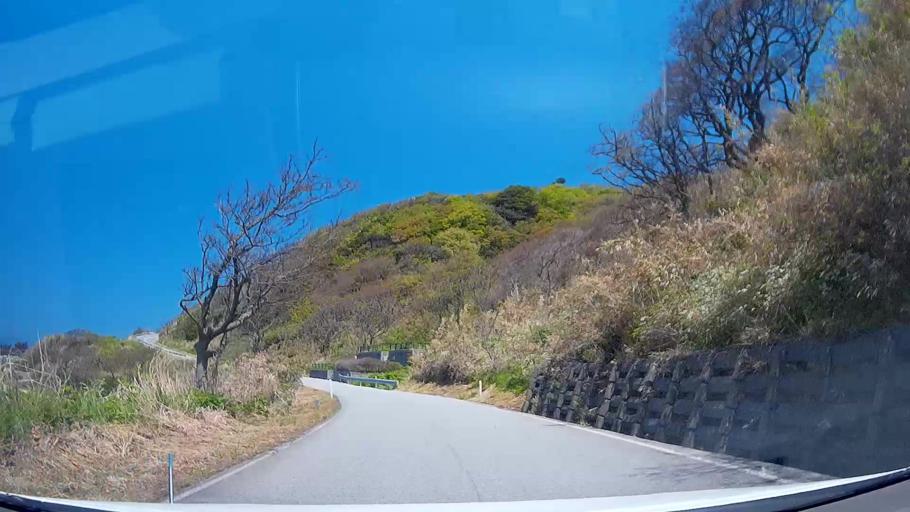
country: JP
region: Ishikawa
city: Nanao
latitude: 37.5221
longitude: 137.2473
